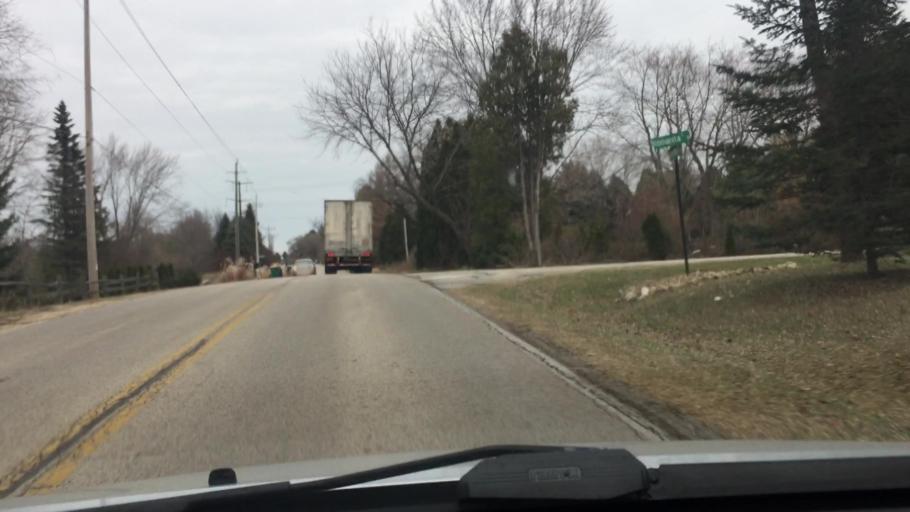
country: US
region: Wisconsin
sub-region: Ozaukee County
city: Cedarburg
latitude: 43.2900
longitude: -87.9662
